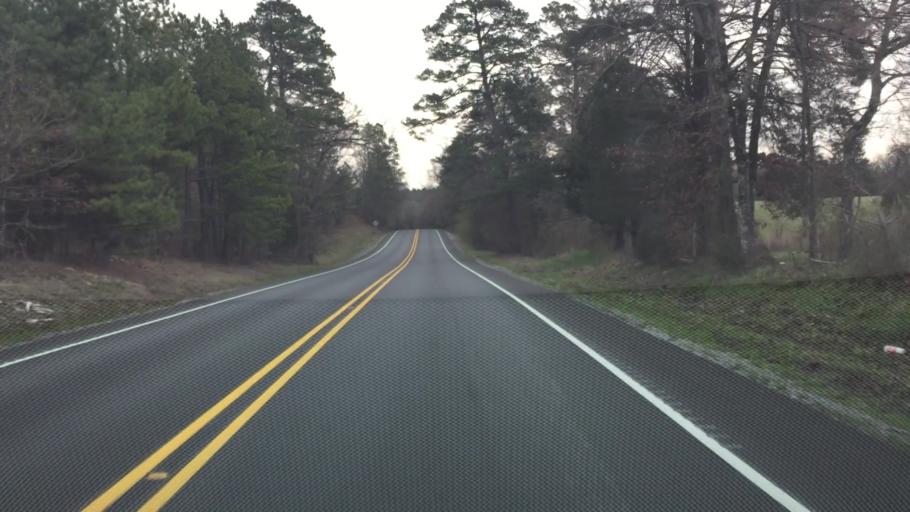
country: US
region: Arkansas
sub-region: Saline County
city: Haskell
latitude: 34.6121
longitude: -92.8052
